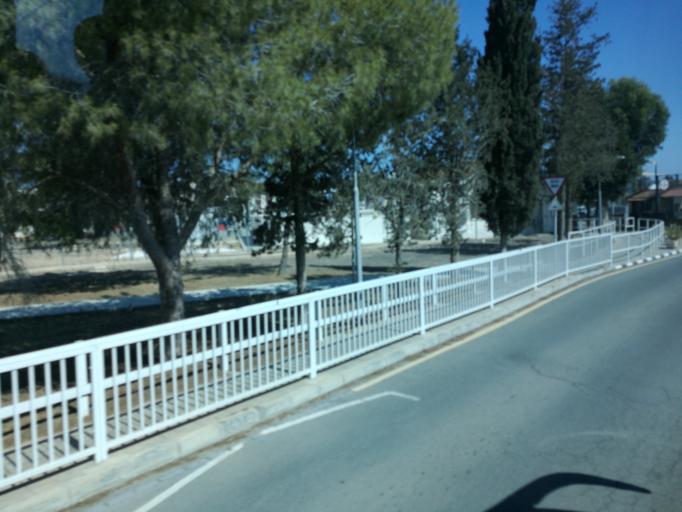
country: CY
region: Ammochostos
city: Acheritou
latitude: 35.0899
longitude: 33.8897
